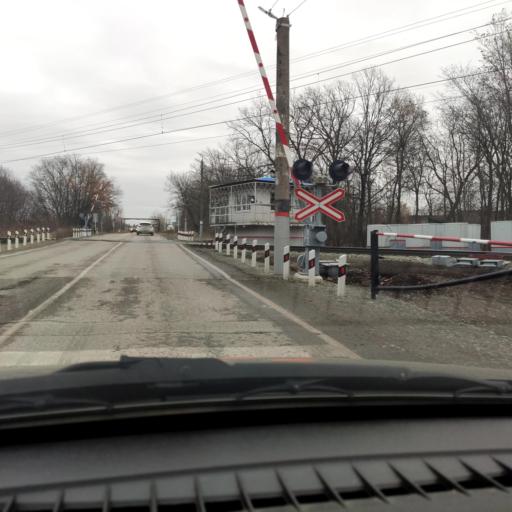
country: RU
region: Samara
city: Zhigulevsk
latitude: 53.3407
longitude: 49.4658
